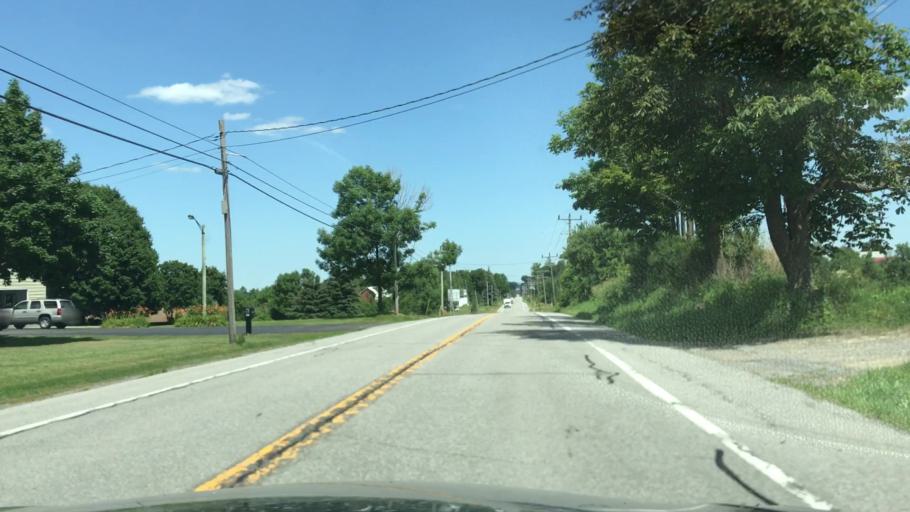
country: US
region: New York
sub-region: Wyoming County
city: Perry
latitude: 42.7443
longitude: -78.0581
